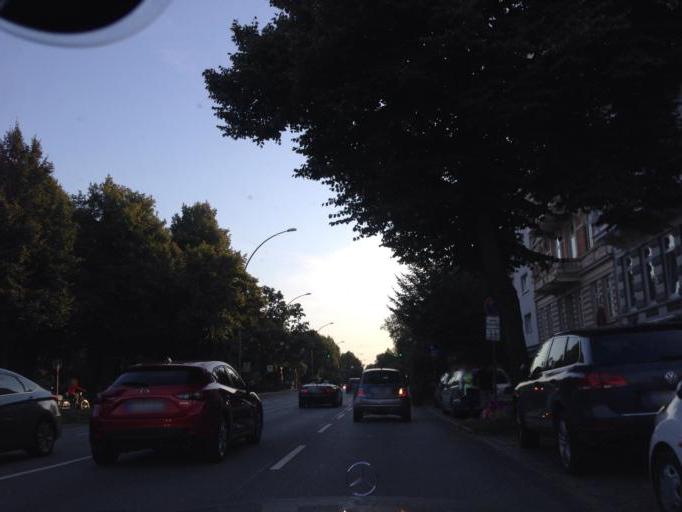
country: DE
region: Hamburg
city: Hamburg
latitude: 53.5666
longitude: 10.0212
